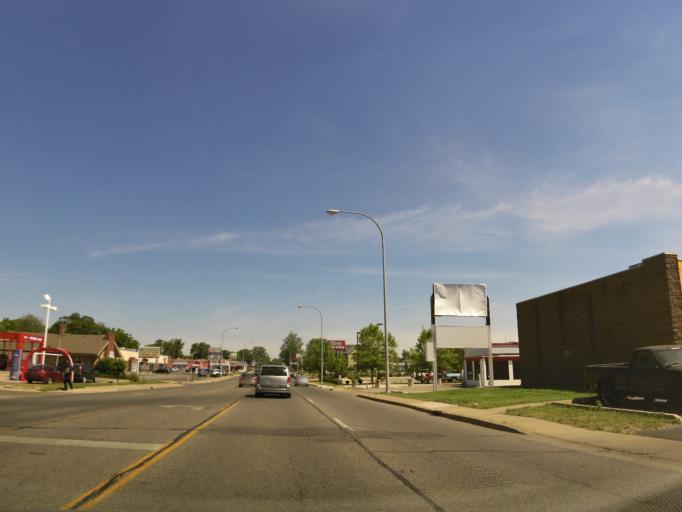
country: US
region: Illinois
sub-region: Vermilion County
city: Danville
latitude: 40.1339
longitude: -87.6356
